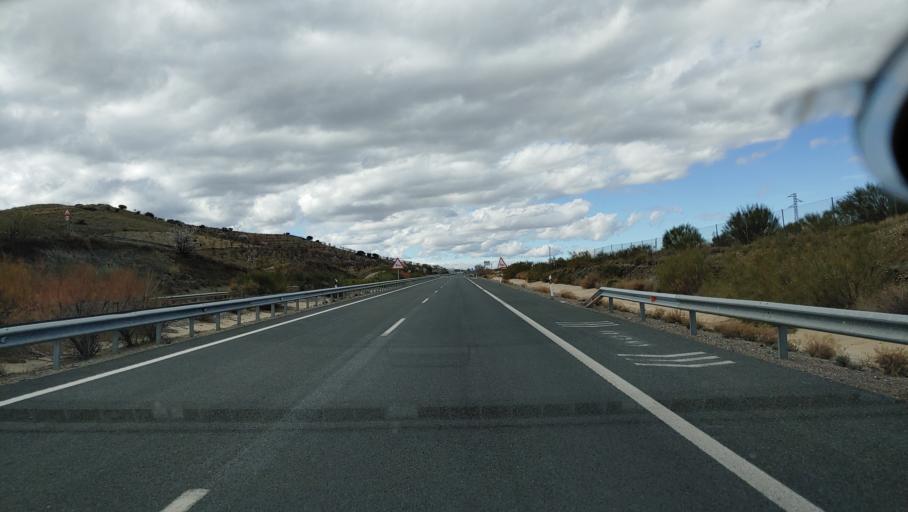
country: ES
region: Andalusia
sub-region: Provincia de Granada
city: Hueneja
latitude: 37.1674
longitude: -2.8970
